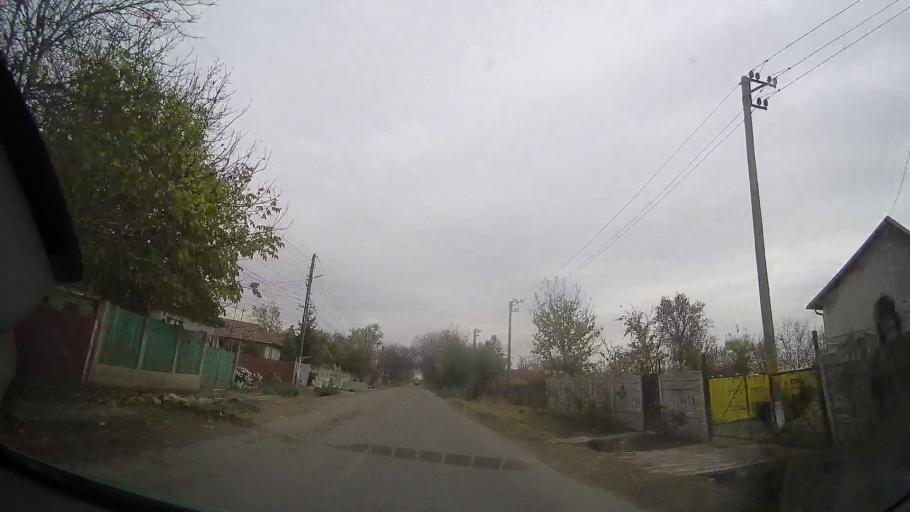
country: RO
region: Prahova
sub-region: Comuna Vadu Sapat
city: Vadu Sapat
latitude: 45.0294
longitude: 26.3906
